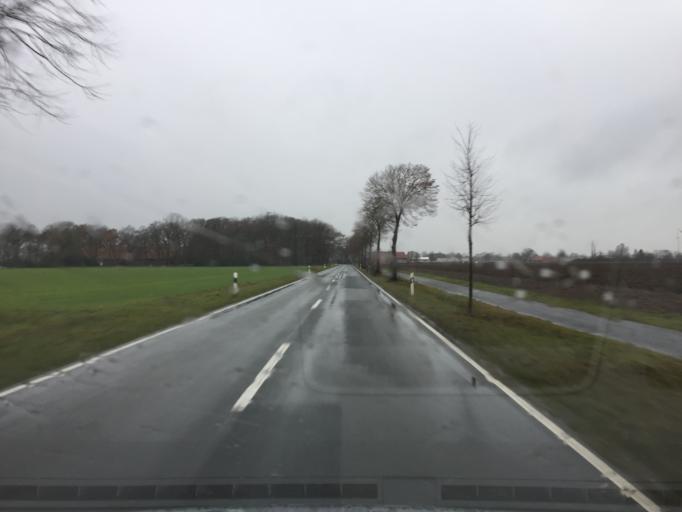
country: DE
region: Lower Saxony
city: Steyerberg
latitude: 52.5974
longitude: 8.9617
